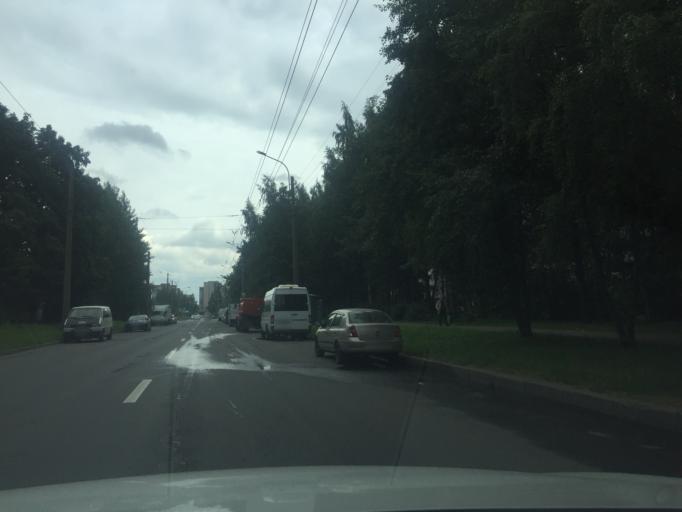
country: RU
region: Leningrad
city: Parnas
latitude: 60.0540
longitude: 30.3680
